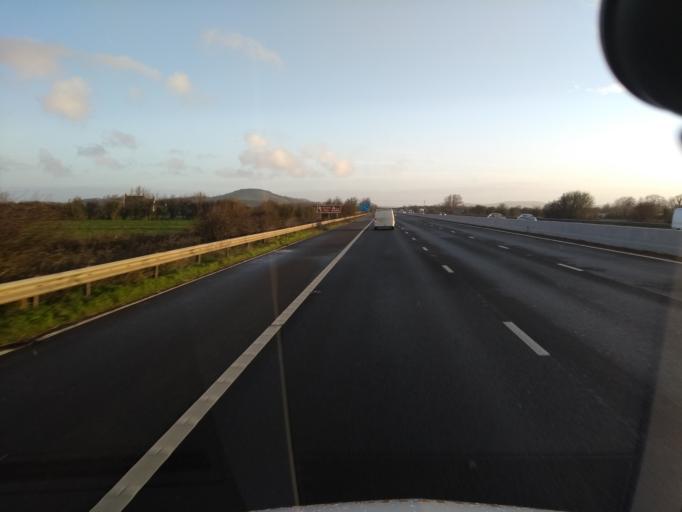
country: GB
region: England
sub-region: Somerset
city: Highbridge
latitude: 51.2244
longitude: -2.9554
